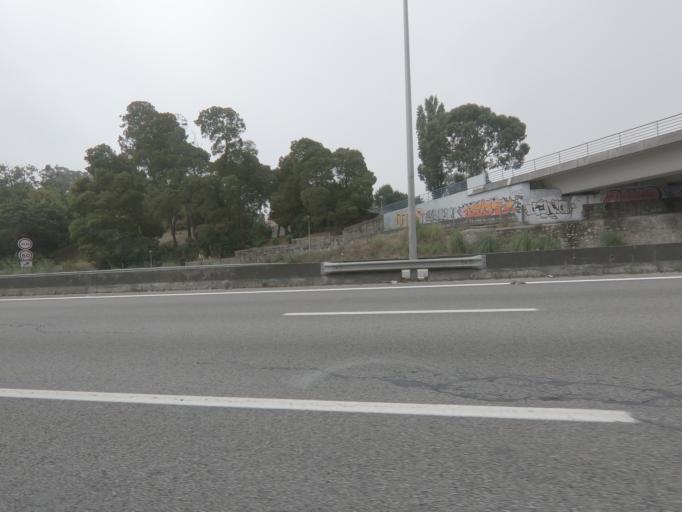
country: PT
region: Porto
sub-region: Matosinhos
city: Leca da Palmeira
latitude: 41.1989
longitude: -8.6865
